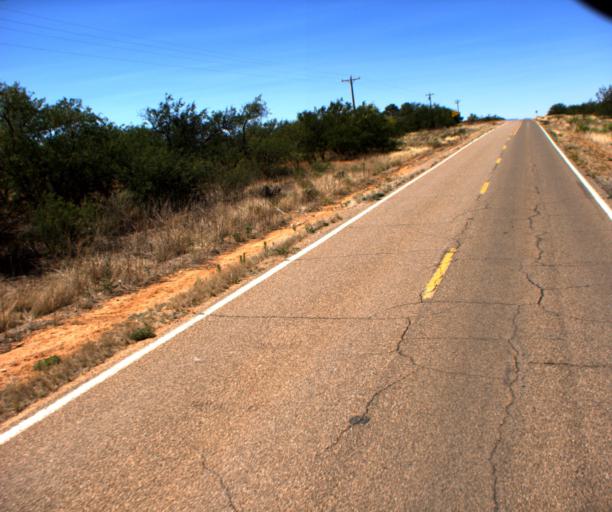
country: US
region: Arizona
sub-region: Santa Cruz County
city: Tubac
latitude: 31.4957
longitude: -111.5461
